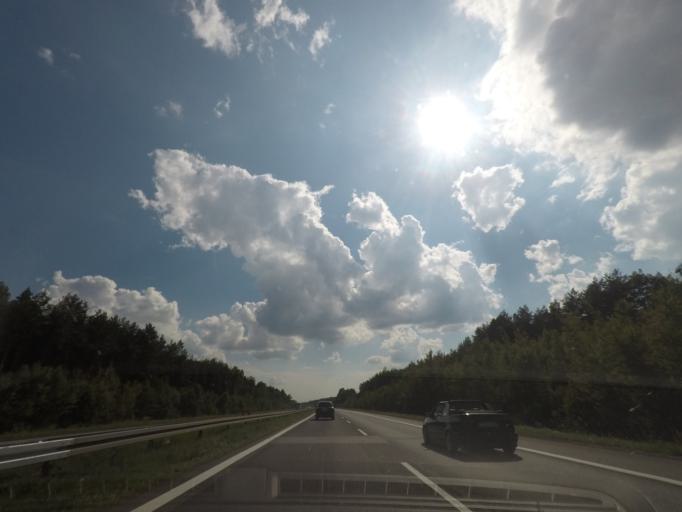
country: PL
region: Silesian Voivodeship
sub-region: Powiat czestochowski
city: Borowno
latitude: 51.0173
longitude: 19.3119
